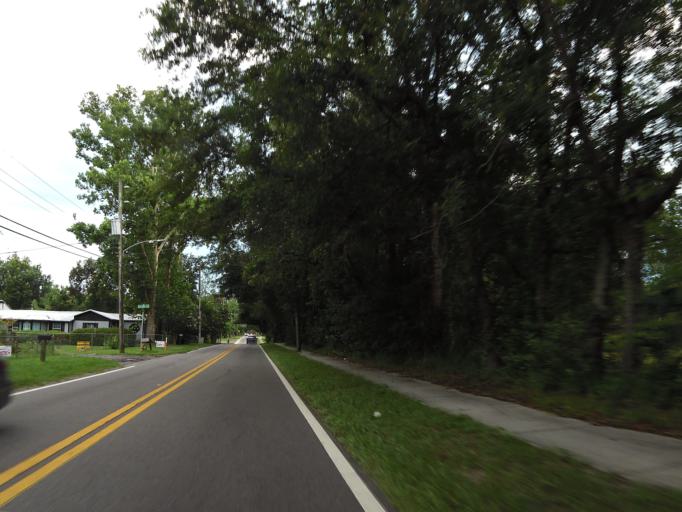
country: US
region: Florida
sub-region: Duval County
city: Jacksonville
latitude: 30.3061
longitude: -81.7835
